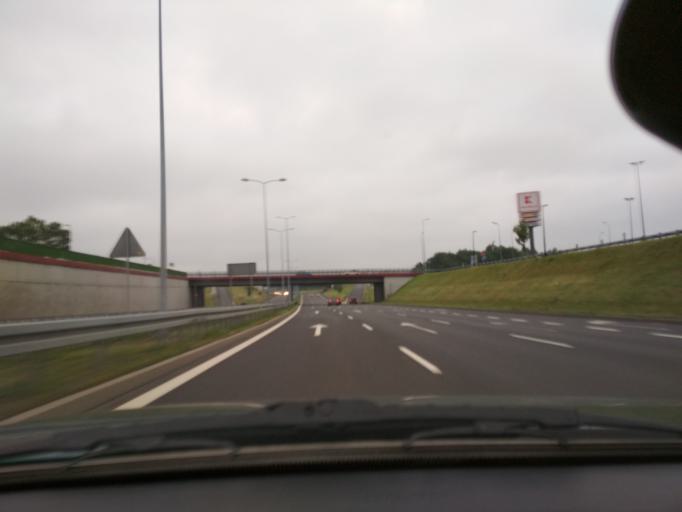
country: PL
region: Silesian Voivodeship
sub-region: Ruda Slaska
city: Ruda Slaska
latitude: 50.2987
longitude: 18.8520
